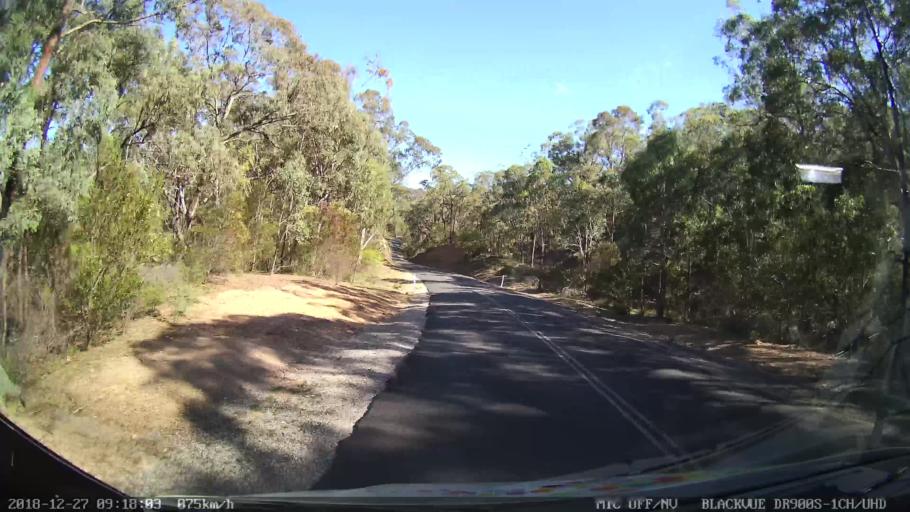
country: AU
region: New South Wales
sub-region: Lithgow
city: Portland
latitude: -33.1310
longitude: 150.0460
